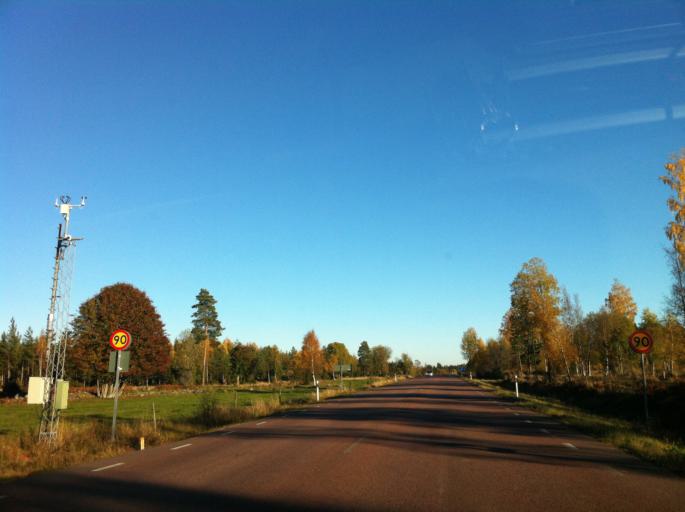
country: SE
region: Dalarna
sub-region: Leksand Municipality
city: Siljansnas
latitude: 60.9224
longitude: 14.8247
